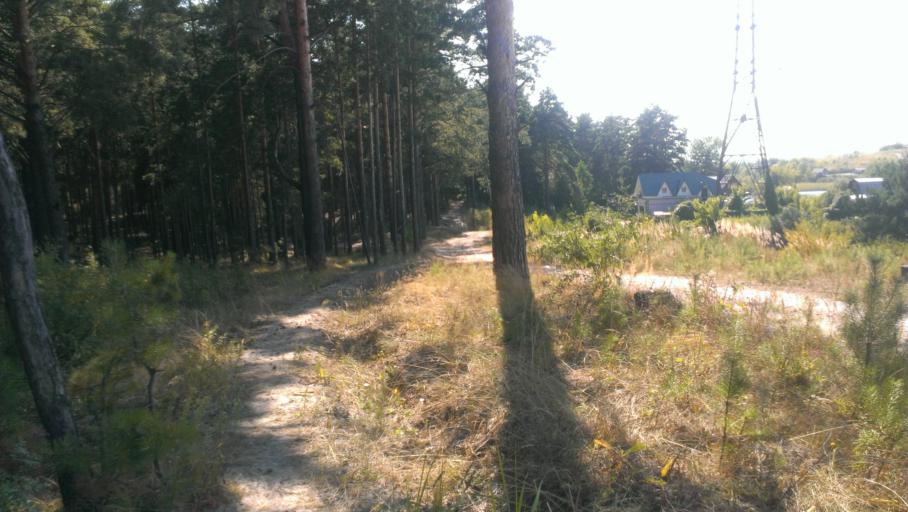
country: RU
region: Altai Krai
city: Novosilikatnyy
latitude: 53.3177
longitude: 83.6798
